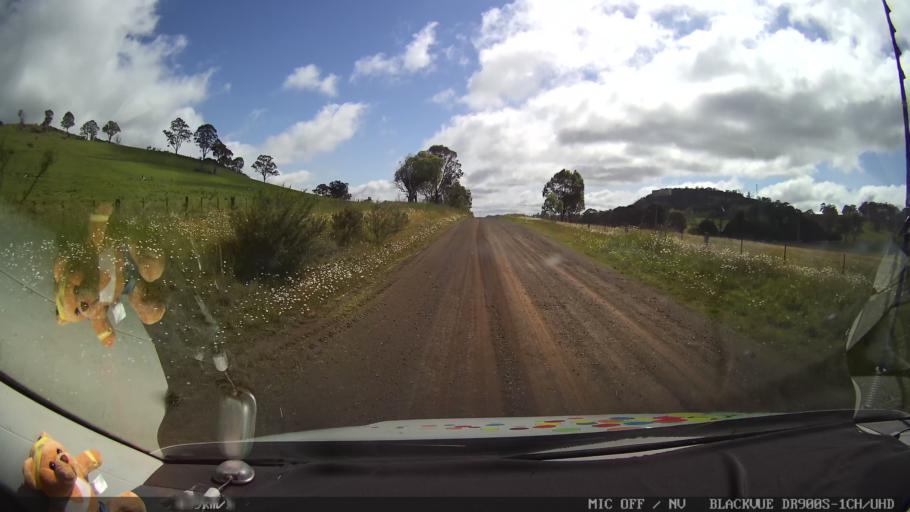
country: AU
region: New South Wales
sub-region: Guyra
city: Guyra
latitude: -30.0077
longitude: 151.6647
